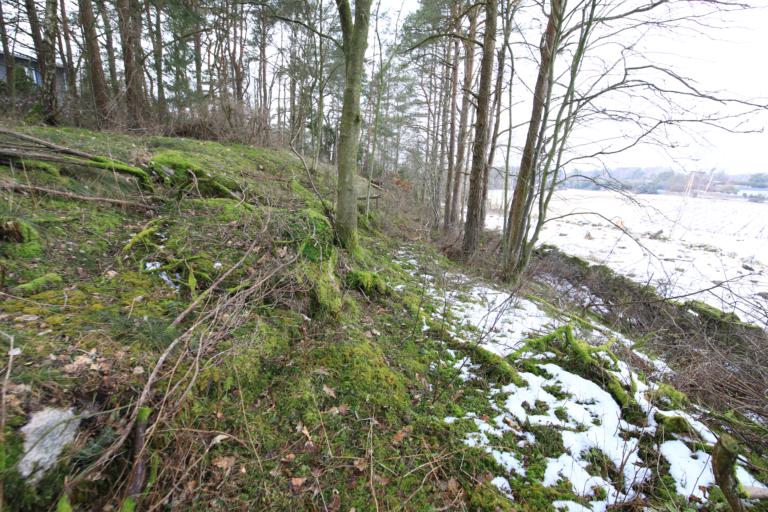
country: SE
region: Halland
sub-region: Kungsbacka Kommun
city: Frillesas
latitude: 57.2172
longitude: 12.1453
